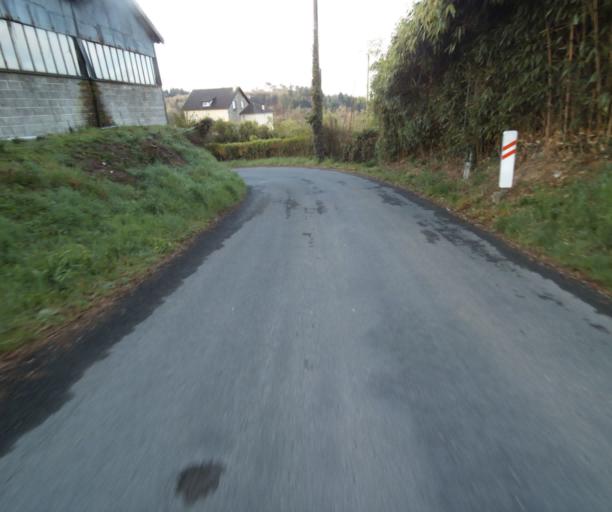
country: FR
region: Limousin
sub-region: Departement de la Correze
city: Correze
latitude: 45.3098
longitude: 1.8435
